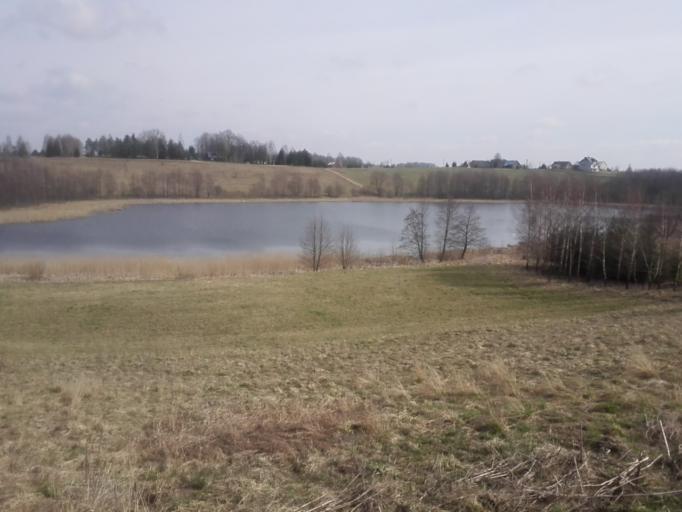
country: PL
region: Podlasie
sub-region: Powiat sejnenski
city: Sejny
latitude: 54.1229
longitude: 23.2828
